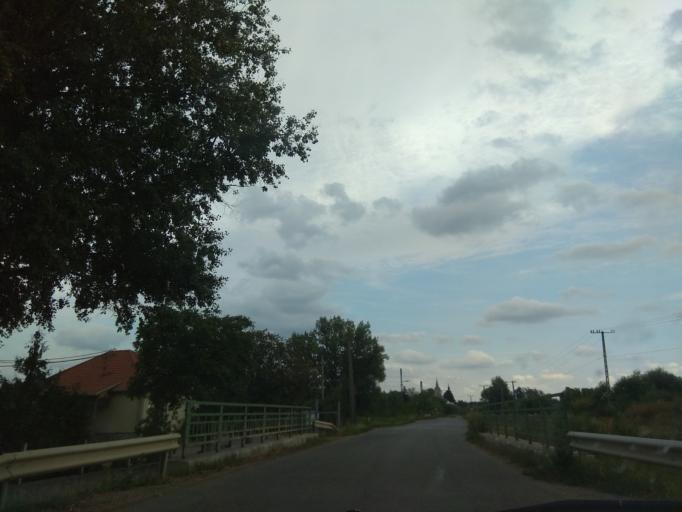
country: HU
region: Borsod-Abauj-Zemplen
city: Gesztely
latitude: 48.1091
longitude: 20.9560
